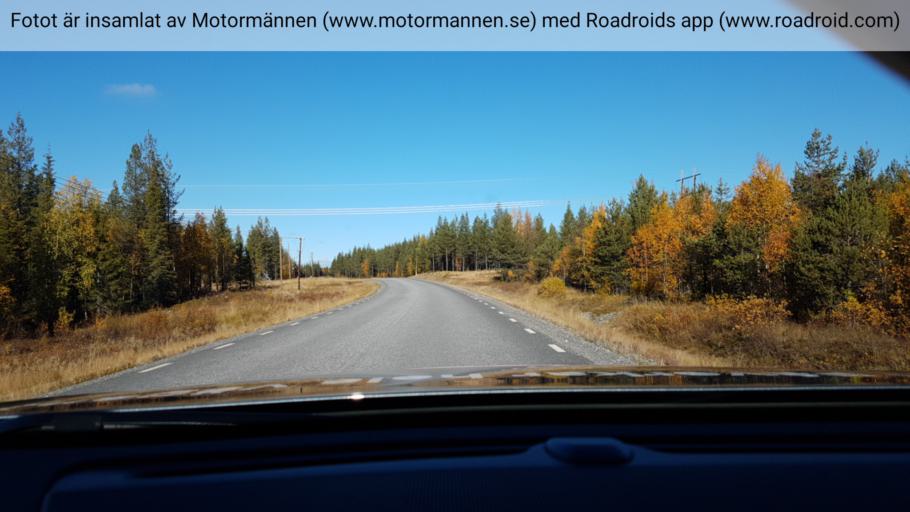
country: SE
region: Norrbotten
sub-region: Gallivare Kommun
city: Gaellivare
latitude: 66.8217
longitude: 21.0428
